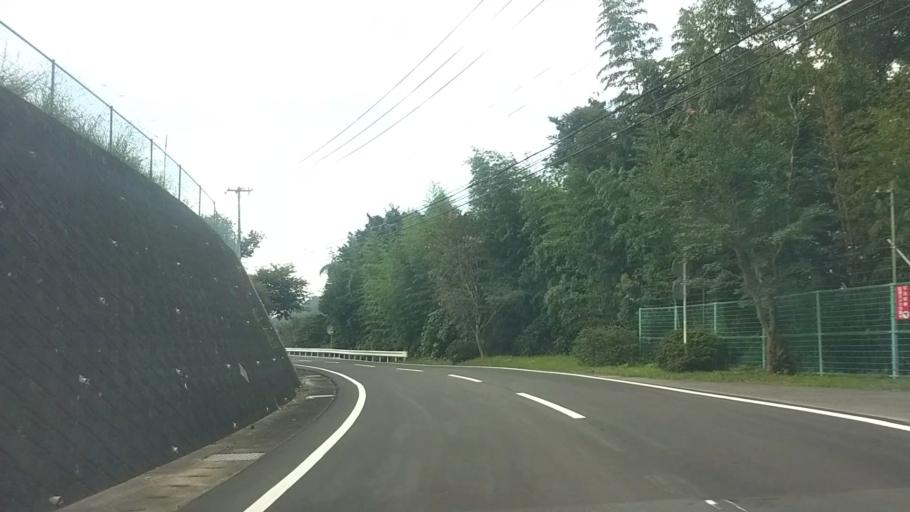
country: JP
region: Shizuoka
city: Ito
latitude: 34.9656
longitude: 138.9723
